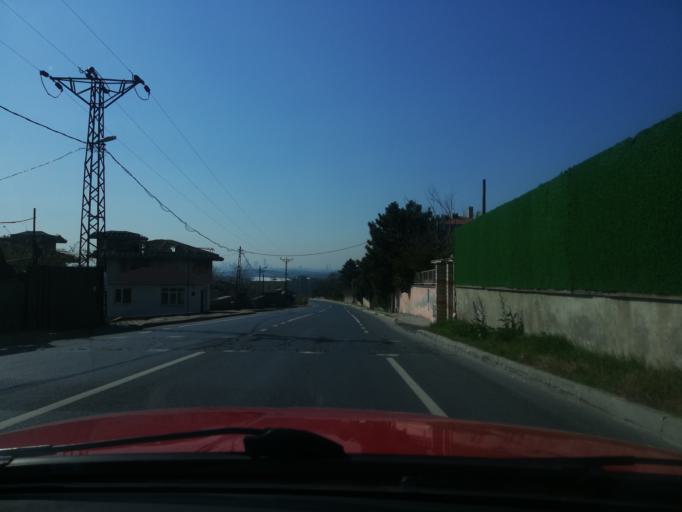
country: TR
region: Istanbul
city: Umraniye
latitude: 41.0738
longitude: 29.1534
